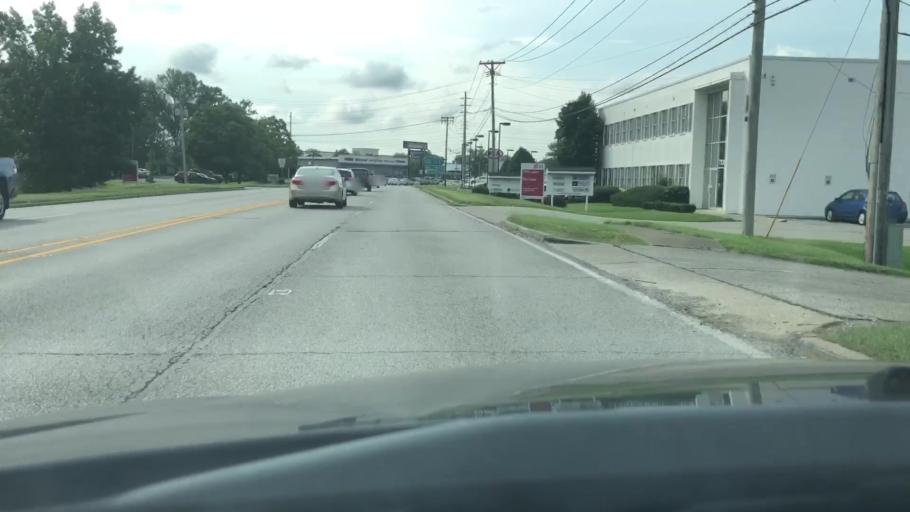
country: US
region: Kentucky
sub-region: Jefferson County
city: Beechwood Village
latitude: 38.2515
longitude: -85.6163
